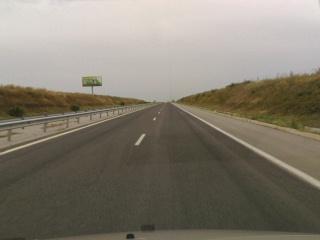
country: BG
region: Stara Zagora
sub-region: Obshtina Nikolaevo
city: Elkhovo
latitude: 42.2986
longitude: 25.4896
